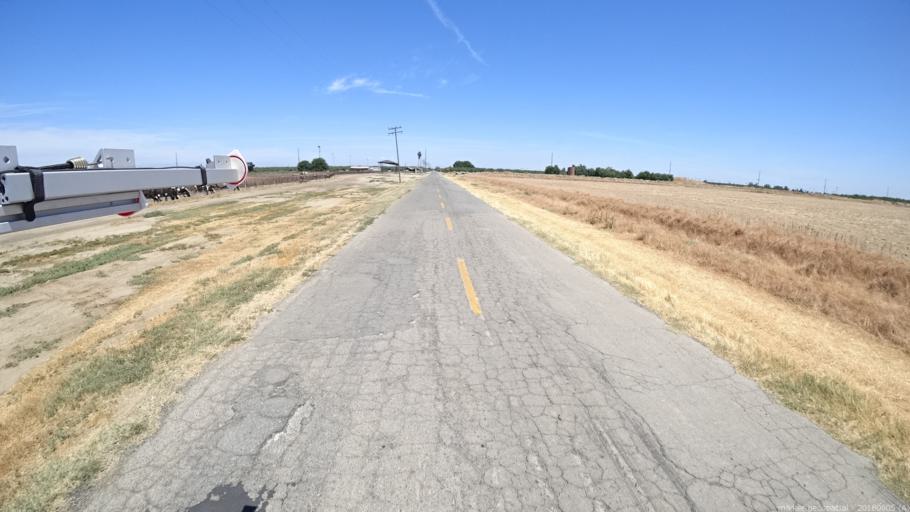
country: US
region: California
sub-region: Madera County
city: Chowchilla
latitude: 37.0907
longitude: -120.3142
